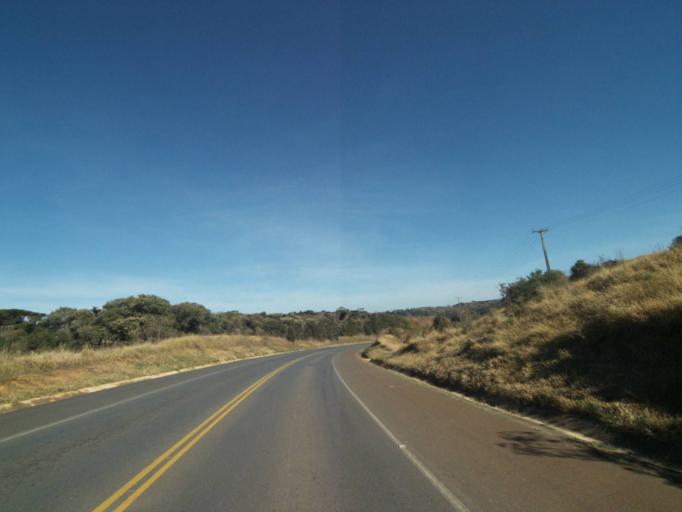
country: BR
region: Parana
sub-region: Tibagi
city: Tibagi
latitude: -24.3964
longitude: -50.3360
